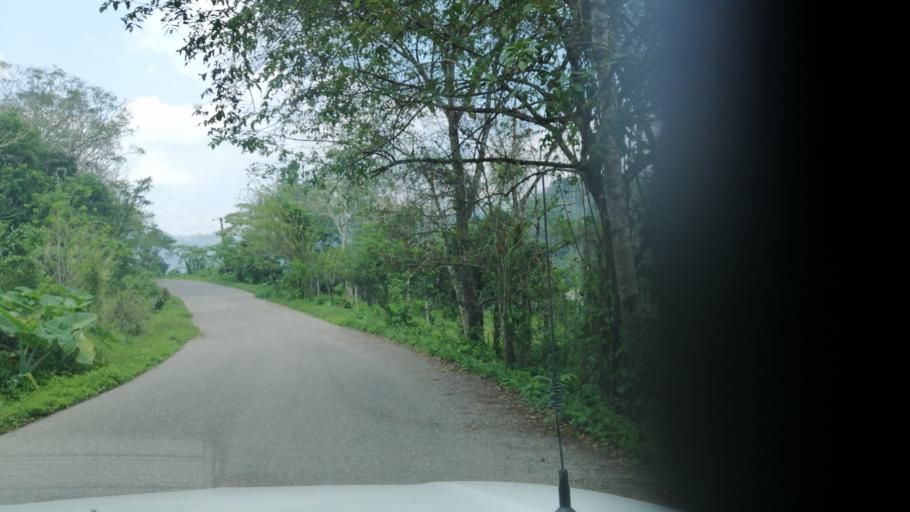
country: MX
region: Chiapas
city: Ostuacan
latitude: 17.3986
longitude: -93.3316
